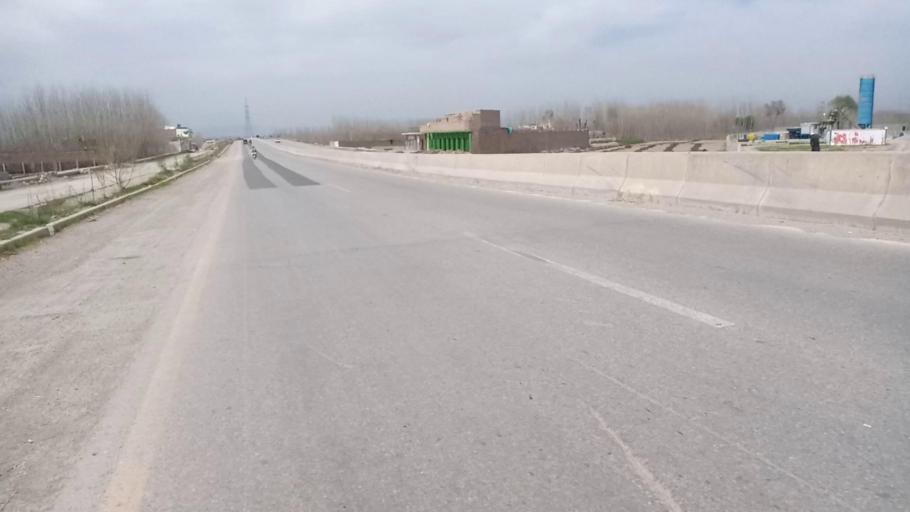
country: PK
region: Khyber Pakhtunkhwa
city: Peshawar
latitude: 34.0512
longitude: 71.6134
